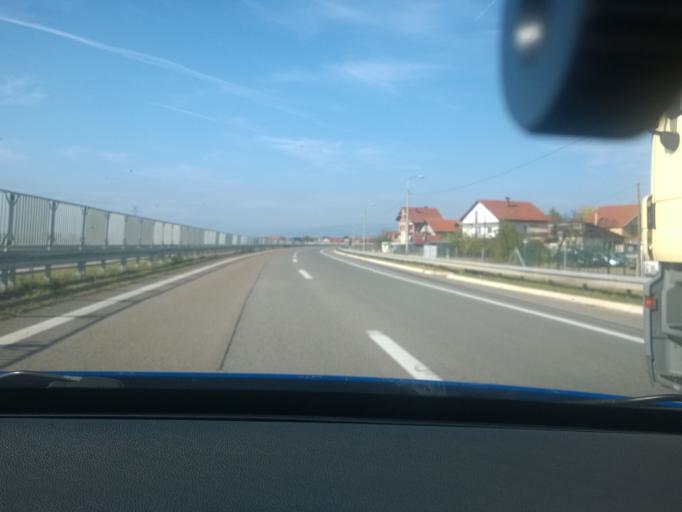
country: RS
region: Central Serbia
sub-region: Nisavski Okrug
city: Nis
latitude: 43.3422
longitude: 21.8893
